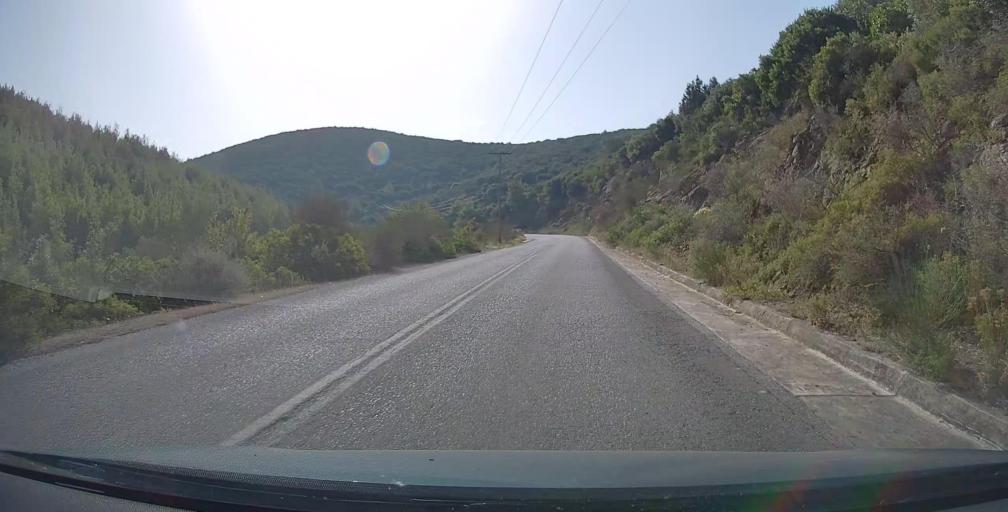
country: GR
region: Central Macedonia
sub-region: Nomos Chalkidikis
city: Sykia
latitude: 39.9615
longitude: 23.9402
